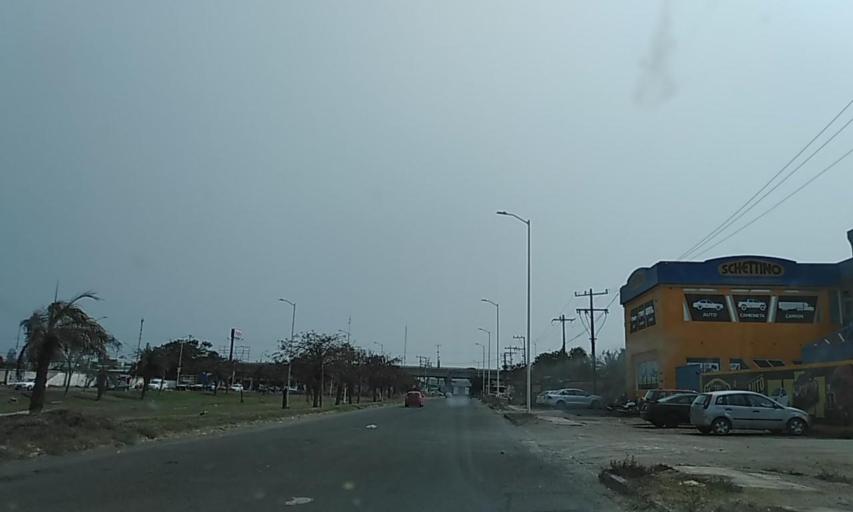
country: MX
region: Veracruz
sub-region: Veracruz
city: Las Amapolas
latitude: 19.1601
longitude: -96.1948
